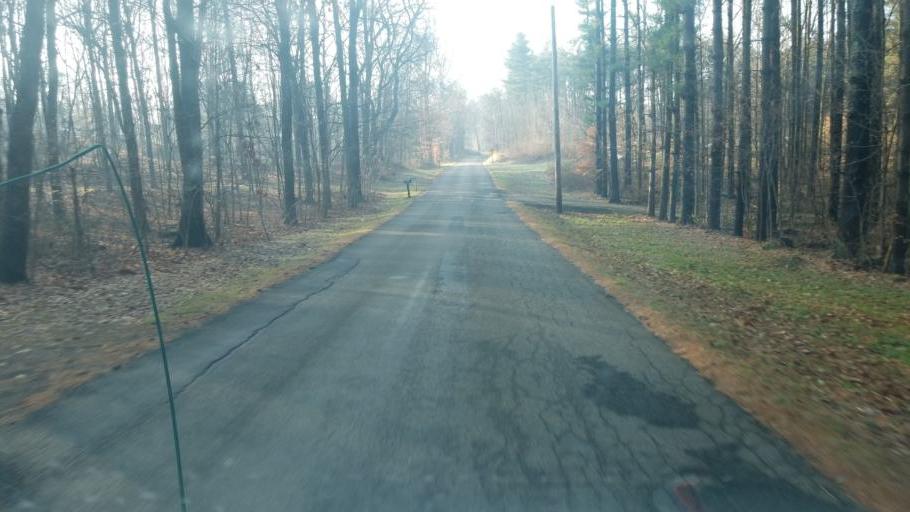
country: US
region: Ohio
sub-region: Knox County
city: Gambier
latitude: 40.4356
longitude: -82.3788
